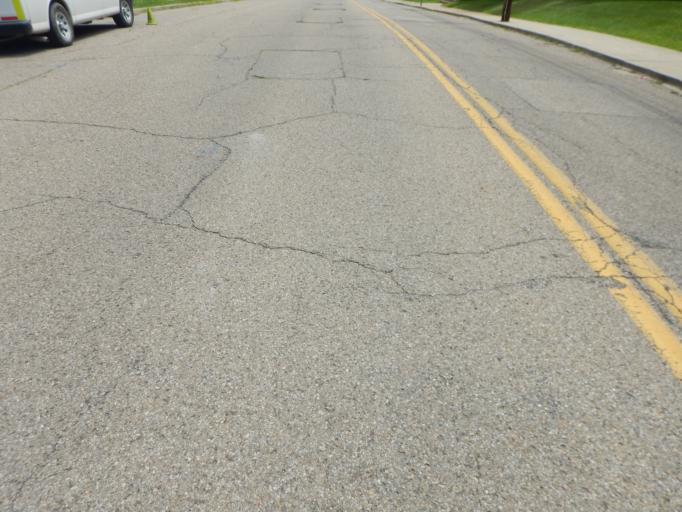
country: US
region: Ohio
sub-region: Muskingum County
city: Zanesville
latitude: 39.9398
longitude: -82.0006
